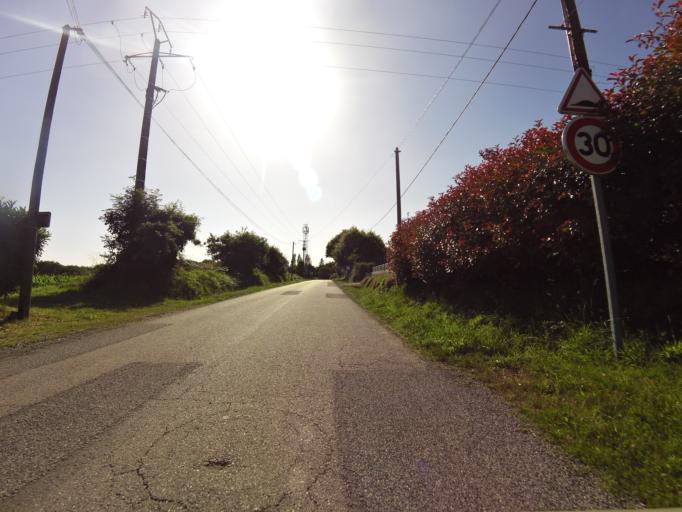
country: FR
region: Brittany
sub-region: Departement du Morbihan
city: Caden
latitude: 47.6307
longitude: -2.2907
